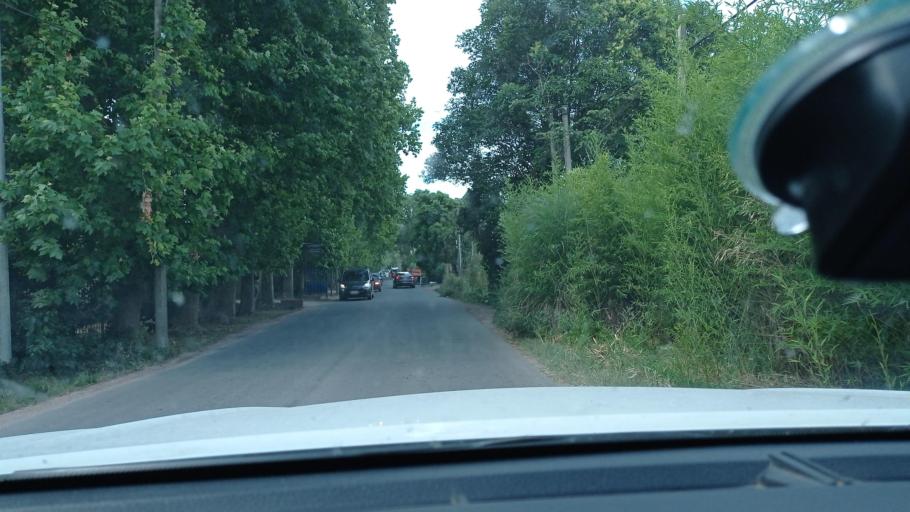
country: UY
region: Canelones
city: La Paz
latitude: -34.8149
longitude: -56.1949
